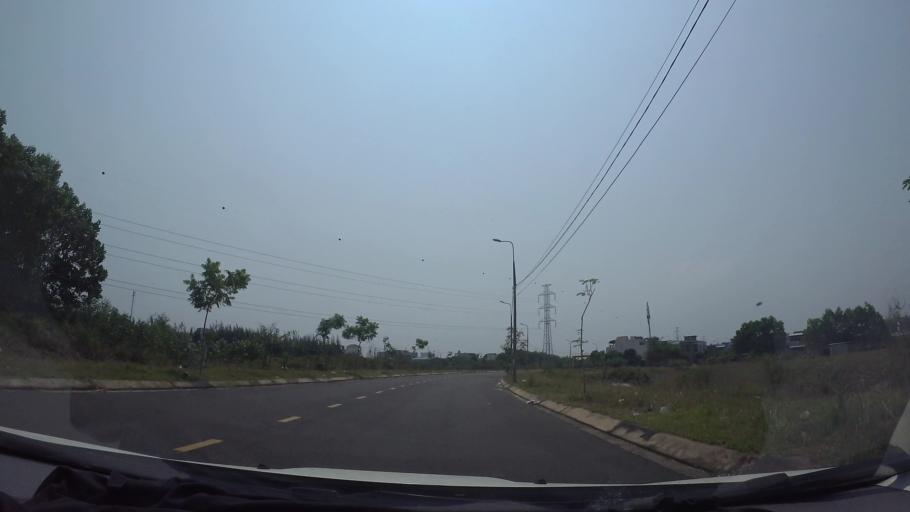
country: VN
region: Da Nang
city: Cam Le
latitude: 15.9951
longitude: 108.2041
